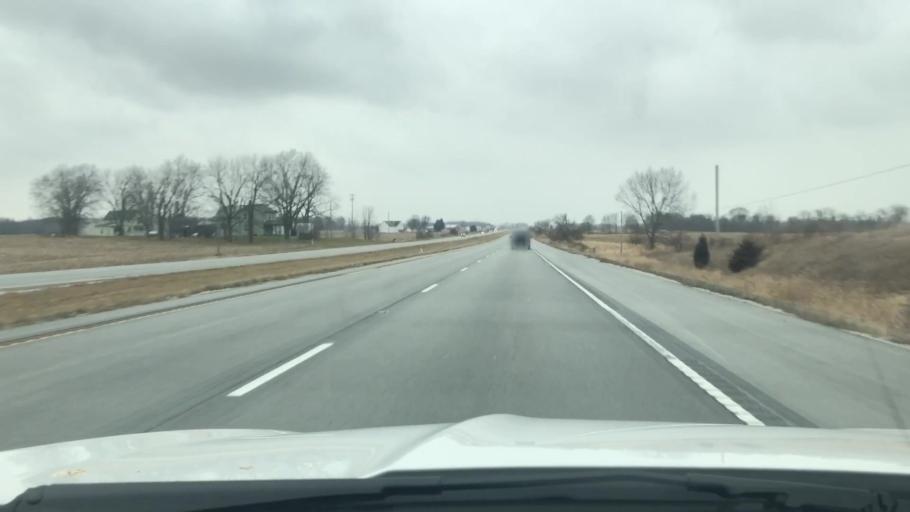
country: US
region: Indiana
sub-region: Miami County
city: Peru
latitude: 40.8531
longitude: -86.1293
